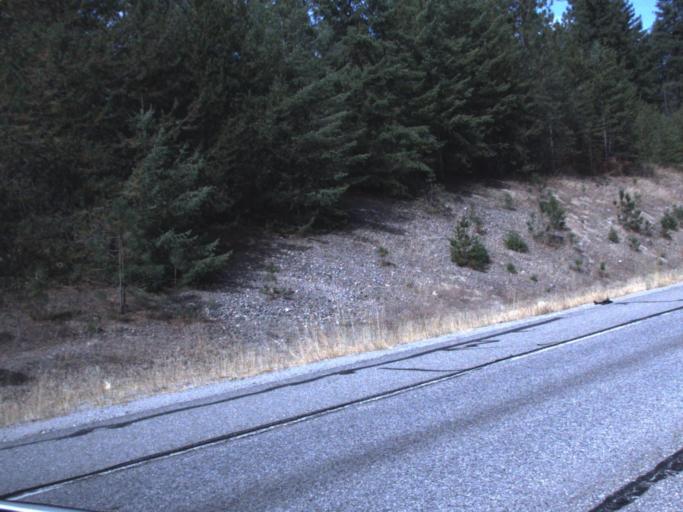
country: US
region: Washington
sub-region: Stevens County
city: Chewelah
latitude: 48.1334
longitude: -117.6550
